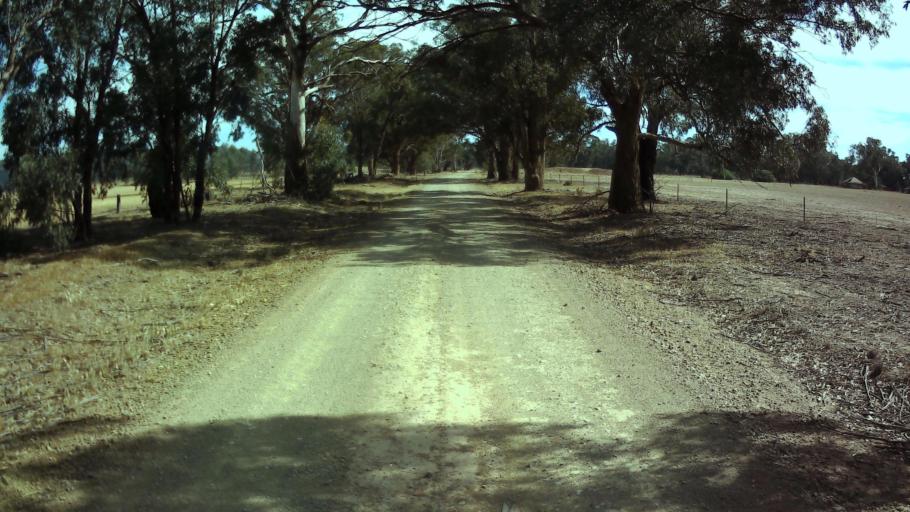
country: AU
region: New South Wales
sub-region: Weddin
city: Grenfell
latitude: -33.6956
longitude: 148.3030
